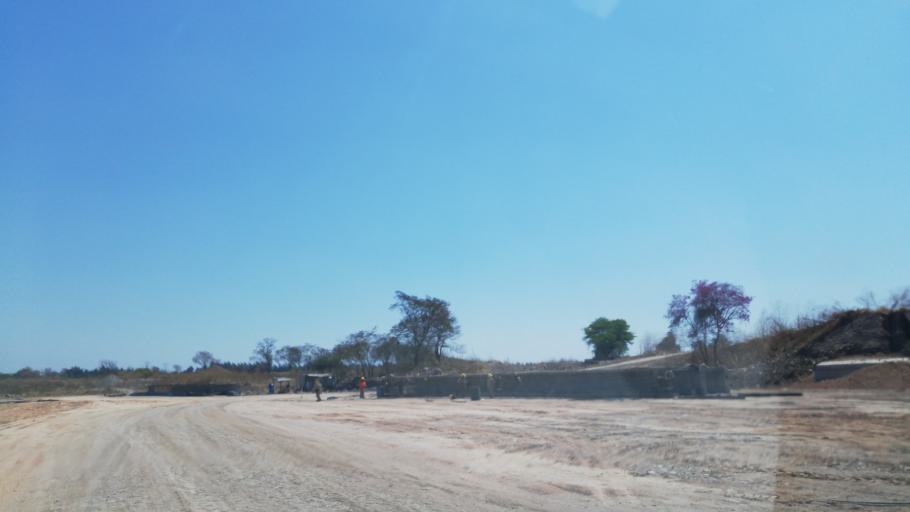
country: AR
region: Salta
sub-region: Departamento de General Guemes
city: General Martin Miguel de Guemes
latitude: -24.5622
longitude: -65.0793
